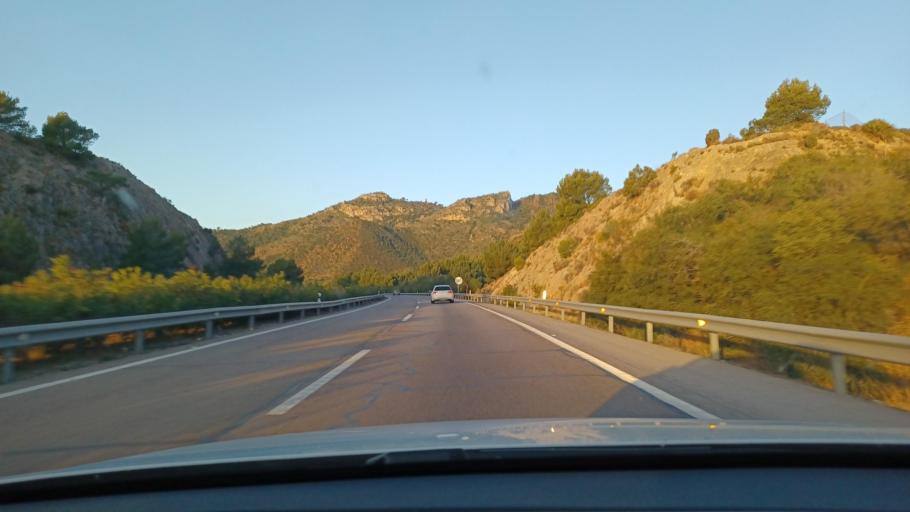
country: ES
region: Valencia
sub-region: Provincia de Castello
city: Benicassim
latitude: 40.0626
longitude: 0.0550
